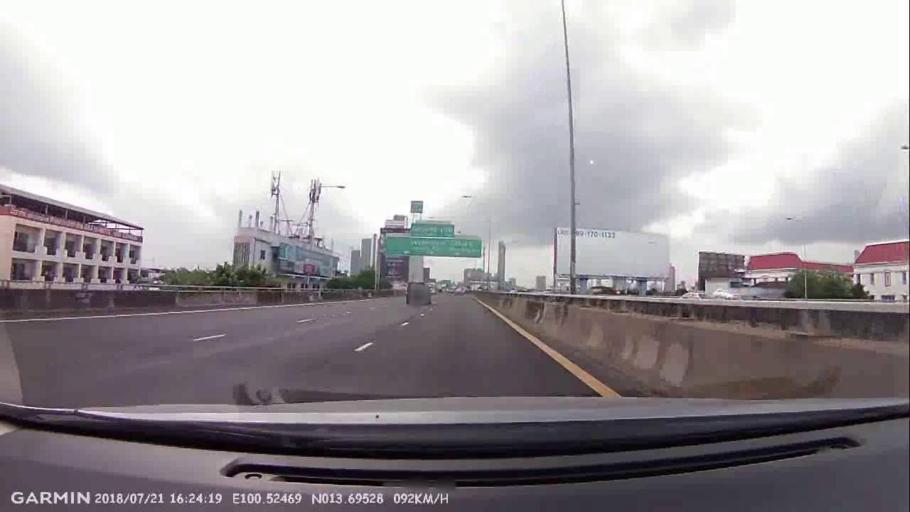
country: TH
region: Bangkok
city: Sathon
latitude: 13.6944
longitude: 100.5251
